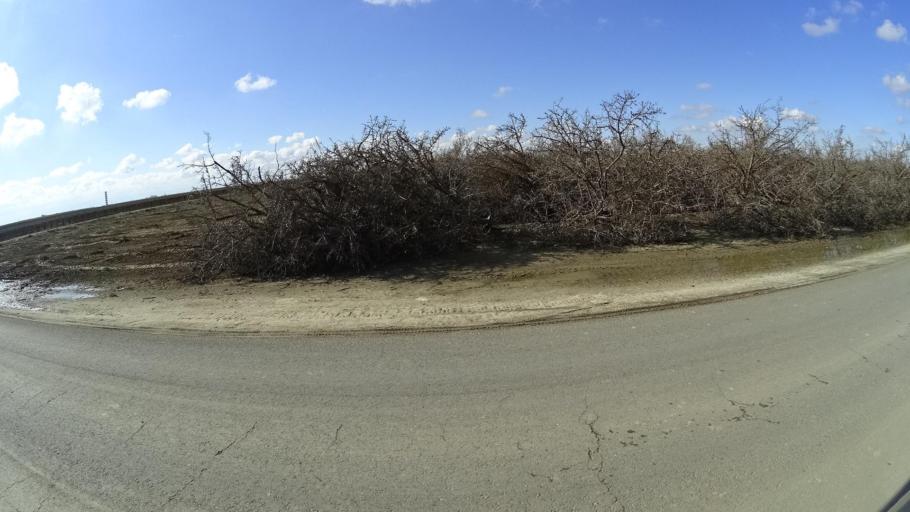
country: US
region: California
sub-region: Kern County
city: Delano
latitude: 35.7398
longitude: -119.3658
